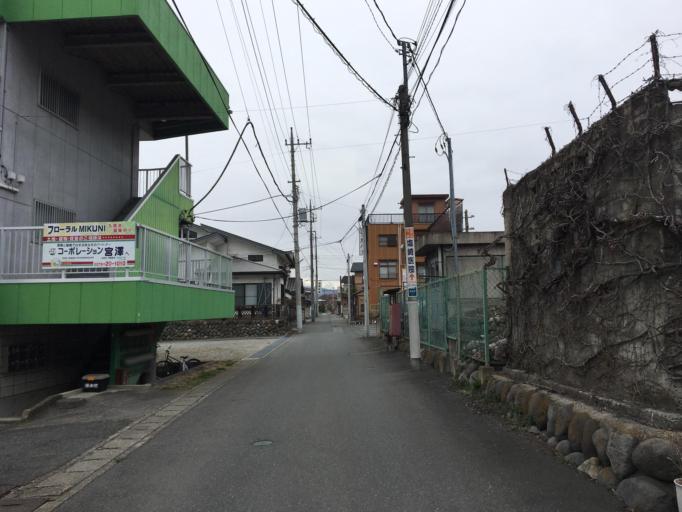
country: JP
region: Gunma
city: Numata
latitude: 36.6435
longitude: 139.0369
